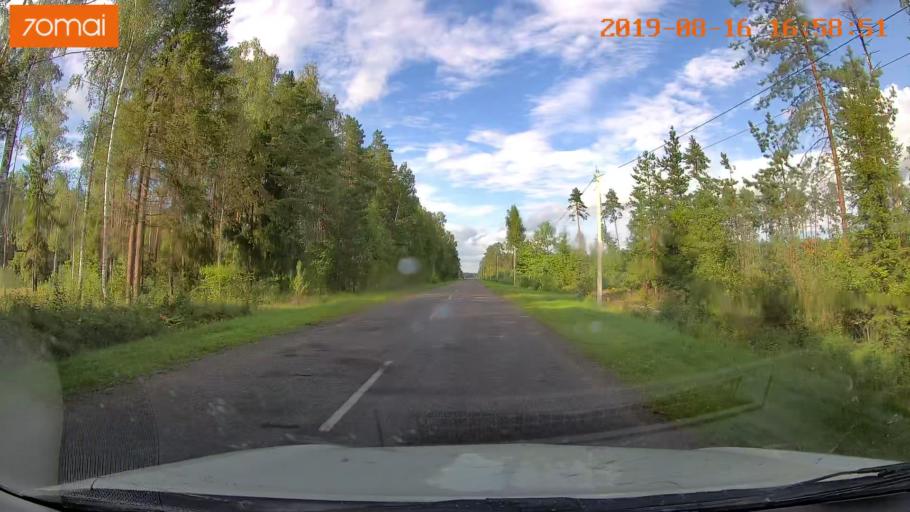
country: BY
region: Mogilev
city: Hlusha
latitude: 53.2748
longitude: 28.8370
